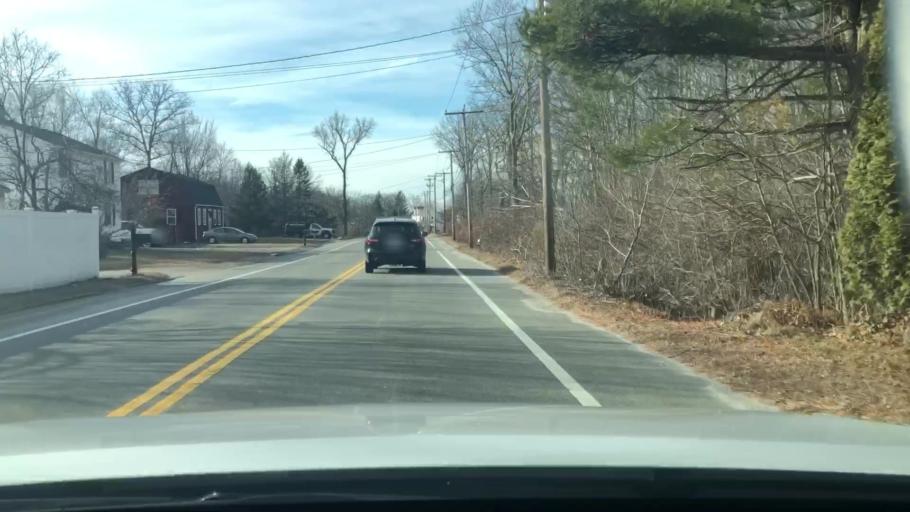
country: US
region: Massachusetts
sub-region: Worcester County
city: Grafton
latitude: 42.2064
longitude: -71.6786
